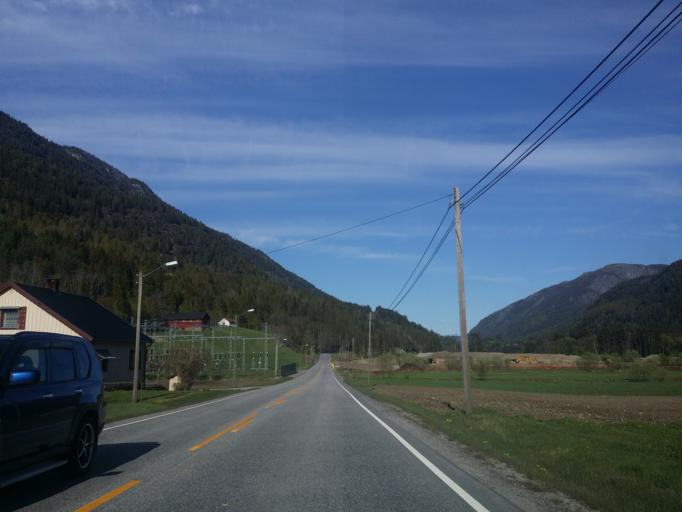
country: NO
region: Telemark
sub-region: Seljord
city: Seljord
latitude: 59.6035
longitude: 8.7095
